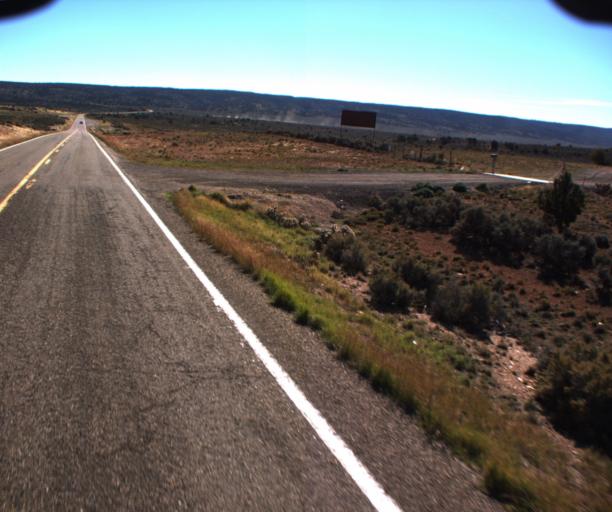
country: US
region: Arizona
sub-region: Coconino County
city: Fredonia
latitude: 36.8558
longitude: -112.3011
